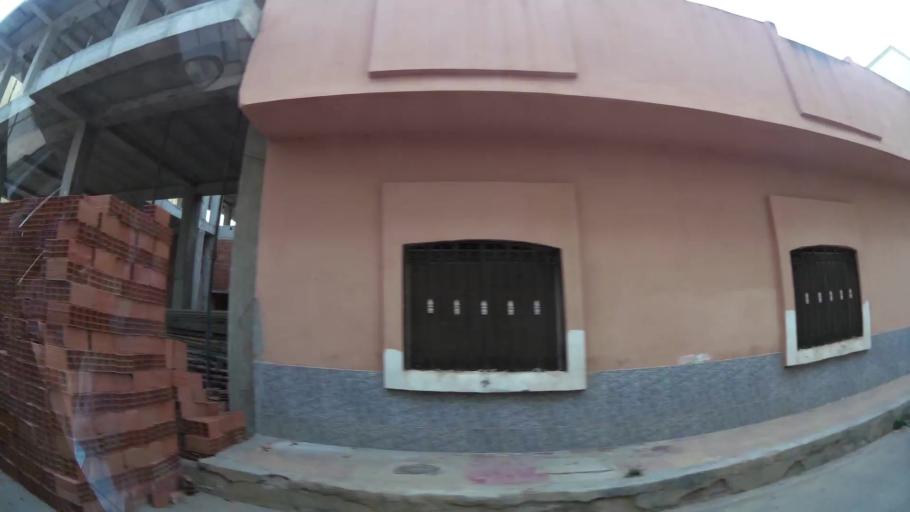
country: MA
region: Oriental
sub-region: Nador
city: Nador
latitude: 35.1625
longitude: -2.9129
